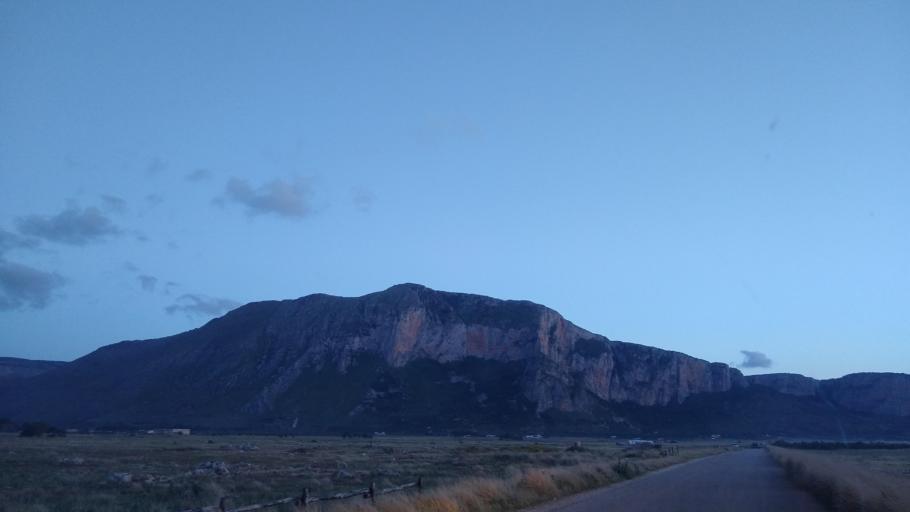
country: IT
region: Sicily
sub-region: Trapani
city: Castelluzzo
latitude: 38.1199
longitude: 12.7230
